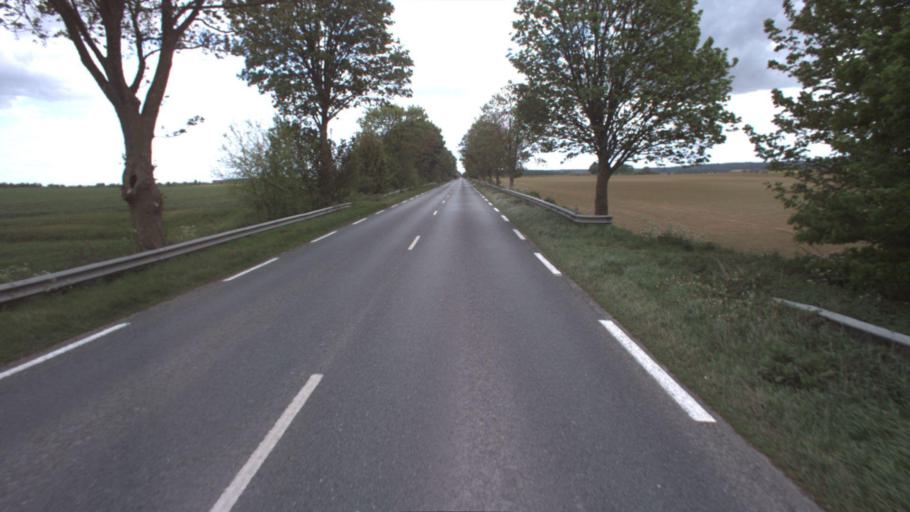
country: FR
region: Picardie
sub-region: Departement de l'Oise
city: Le Plessis-Belleville
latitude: 49.0740
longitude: 2.7671
